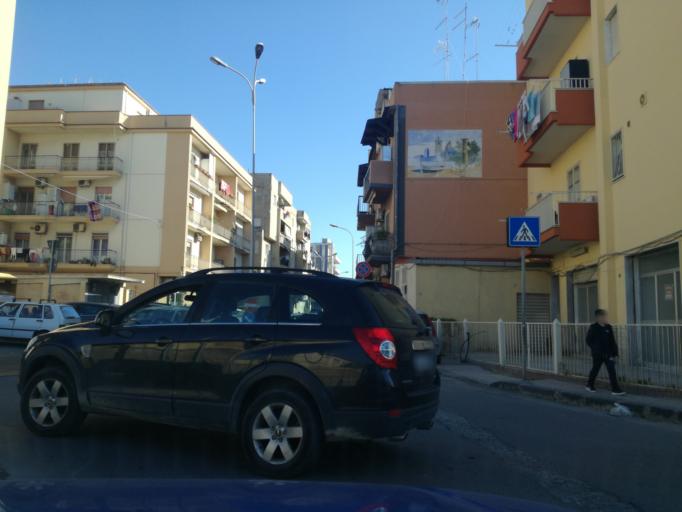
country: IT
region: Sicily
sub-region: Provincia di Caltanissetta
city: Gela
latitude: 37.0718
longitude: 14.2305
